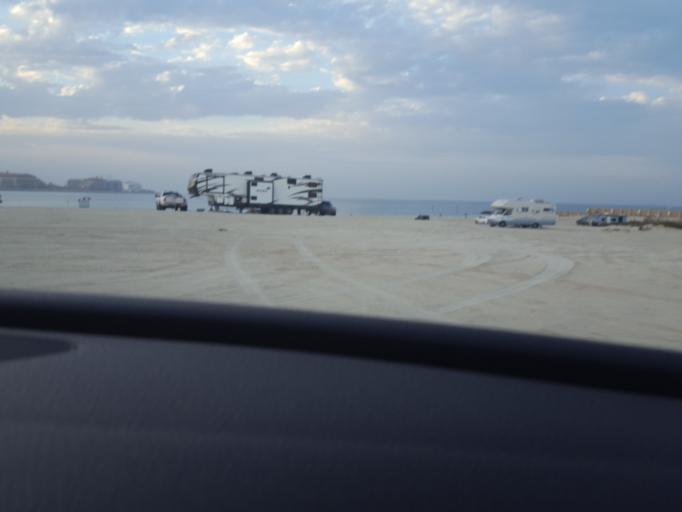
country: AE
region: Dubai
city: Dubai
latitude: 25.1172
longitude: 55.1699
